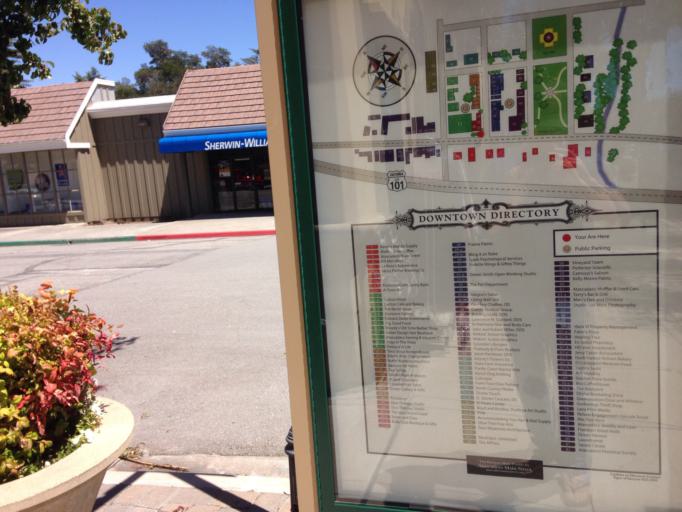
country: US
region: California
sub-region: San Luis Obispo County
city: Atascadero
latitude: 35.4891
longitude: -120.6696
